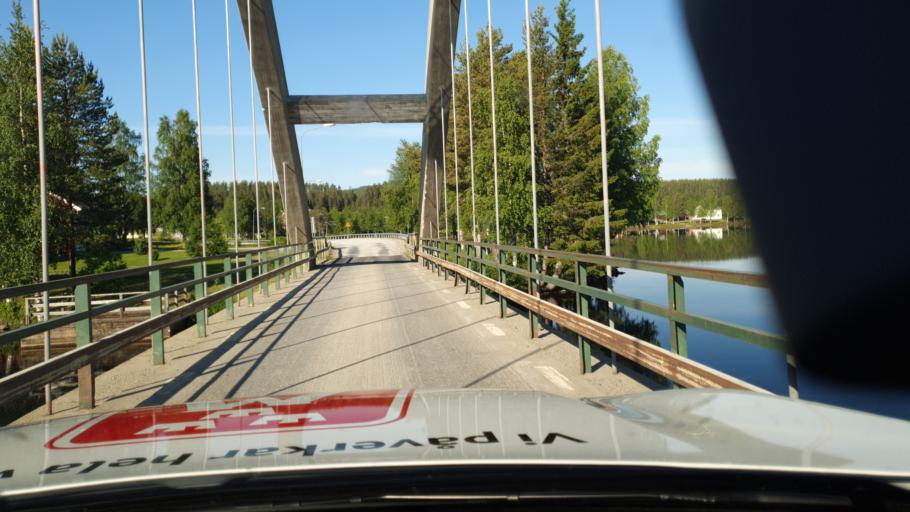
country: SE
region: Vaesterbotten
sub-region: Vindelns Kommun
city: Vindeln
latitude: 64.2025
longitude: 19.4199
